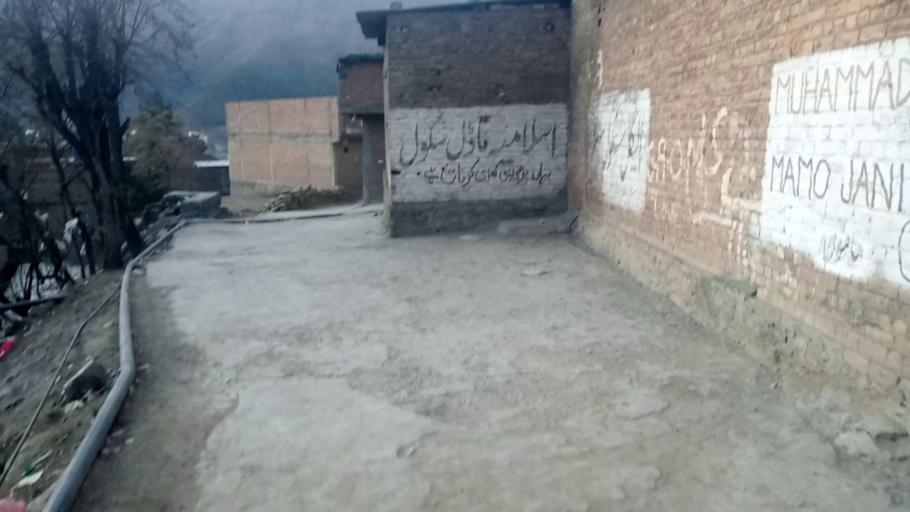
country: PK
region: Khyber Pakhtunkhwa
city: Saidu Sharif
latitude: 34.7379
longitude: 72.3439
